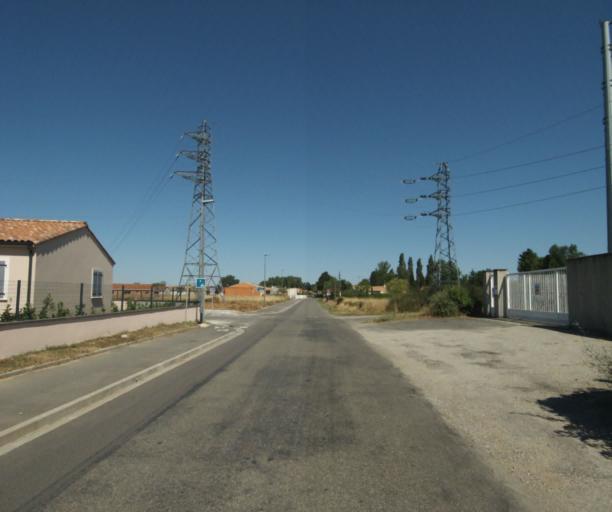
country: FR
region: Midi-Pyrenees
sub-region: Departement de la Haute-Garonne
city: Revel
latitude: 43.4670
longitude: 1.9947
